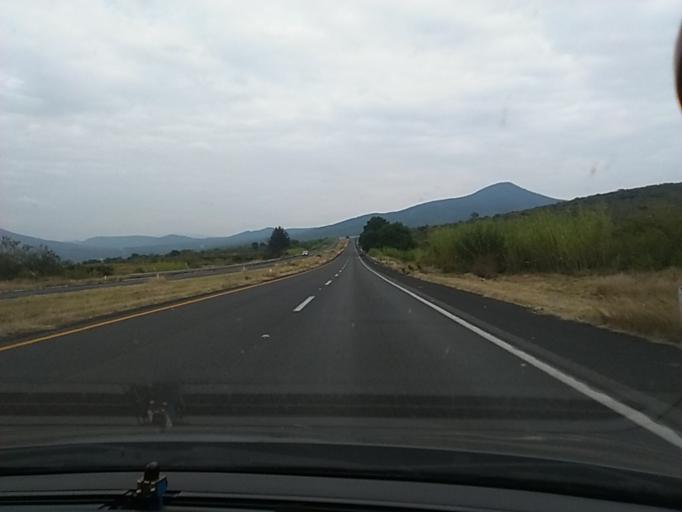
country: MX
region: Michoacan
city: Panindicuaro de la Reforma
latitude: 19.9803
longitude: -101.7829
